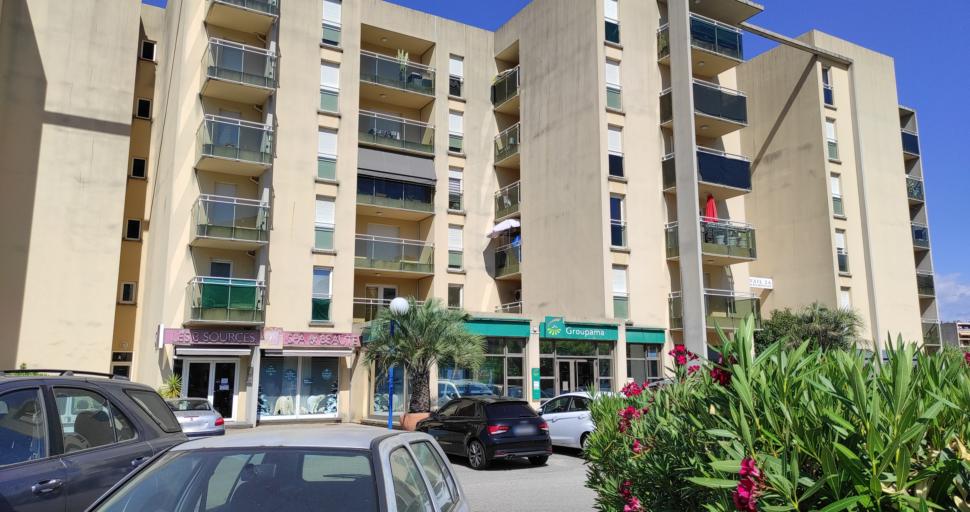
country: FR
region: Corsica
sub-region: Departement de la Corse-du-Sud
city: Ajaccio
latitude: 41.9361
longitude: 8.7361
